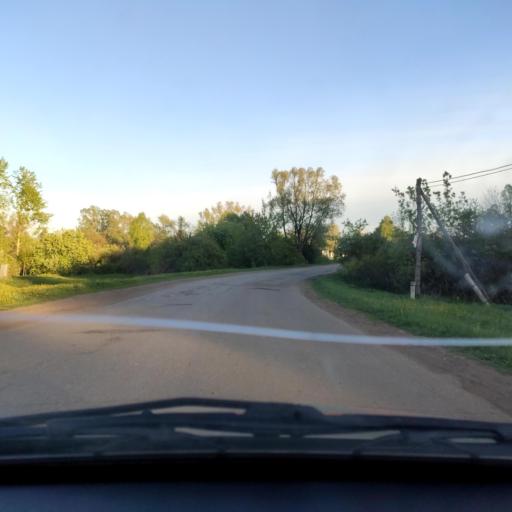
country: RU
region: Bashkortostan
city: Yazykovo
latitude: 55.0416
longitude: 56.1891
